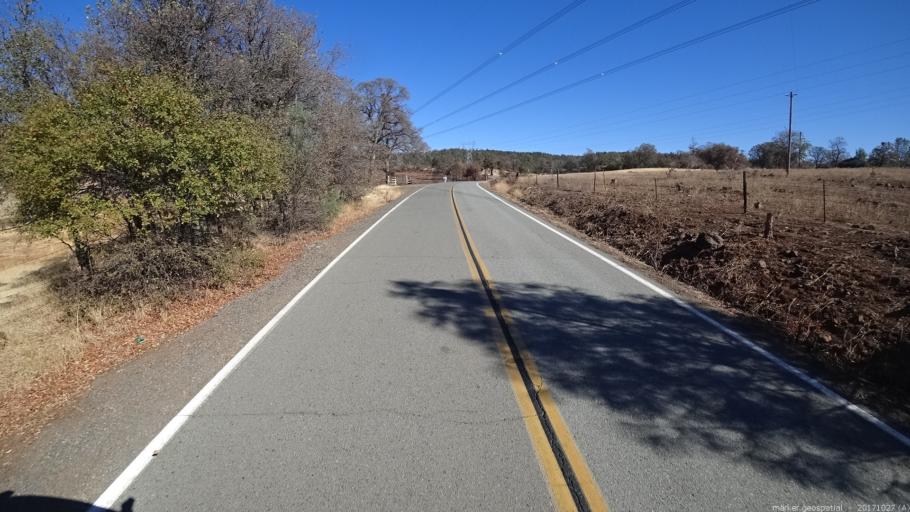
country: US
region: California
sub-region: Shasta County
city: Bella Vista
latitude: 40.7123
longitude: -122.0341
